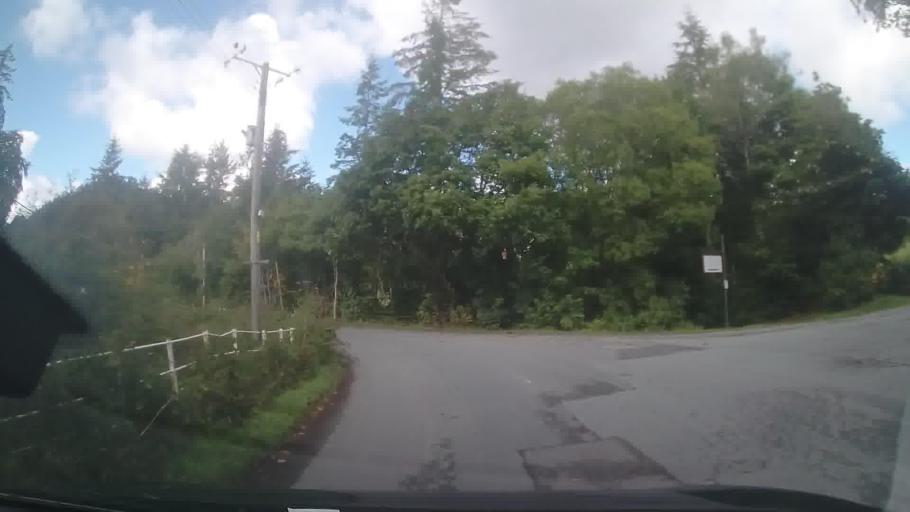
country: GB
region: Wales
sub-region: Sir Powys
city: Llangynog
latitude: 52.7687
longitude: -3.4553
